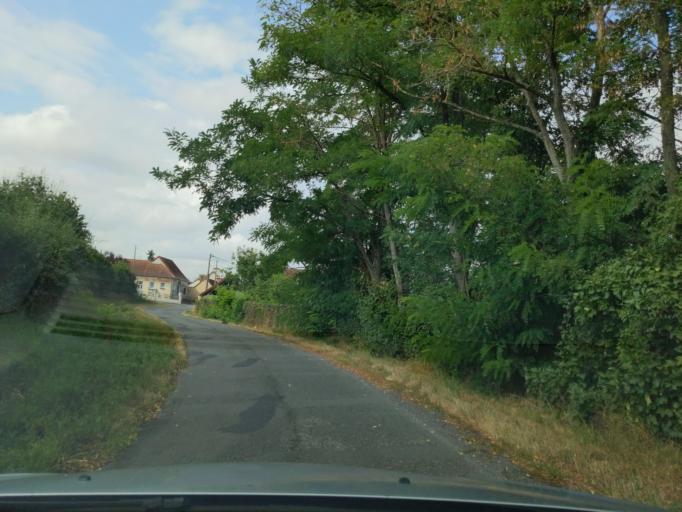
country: FR
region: Bourgogne
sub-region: Departement de Saone-et-Loire
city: Bourbon-Lancy
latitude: 46.6328
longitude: 3.7244
